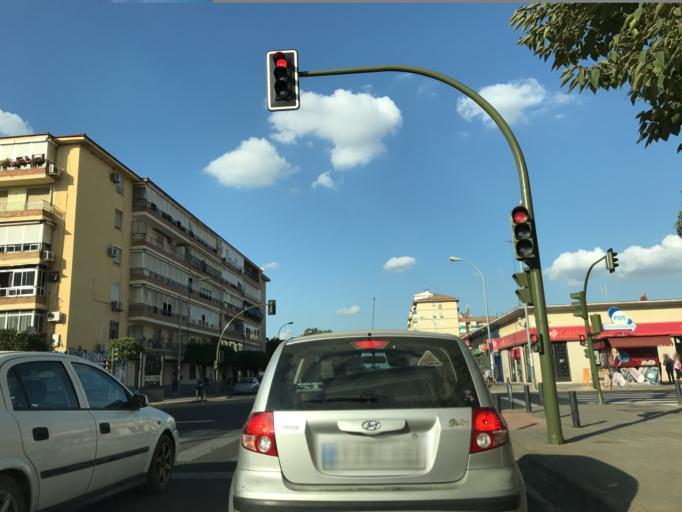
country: ES
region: Andalusia
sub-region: Provincia de Sevilla
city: Sevilla
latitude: 37.4101
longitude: -5.9267
